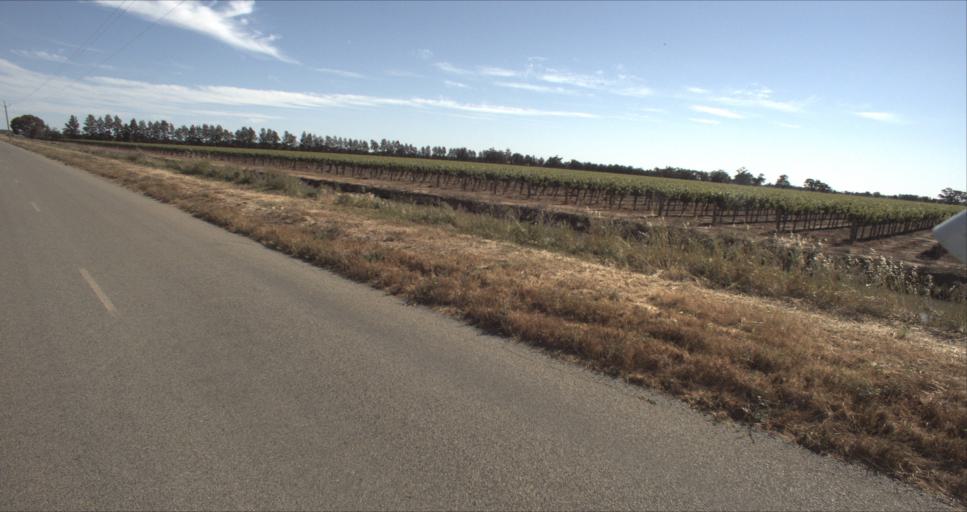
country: AU
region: New South Wales
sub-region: Leeton
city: Leeton
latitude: -34.5816
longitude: 146.3797
